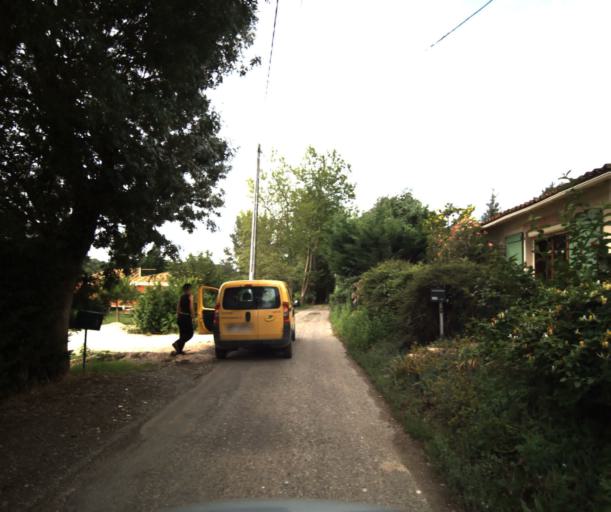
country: FR
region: Midi-Pyrenees
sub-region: Departement de la Haute-Garonne
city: Lacasse
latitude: 43.3906
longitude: 1.2394
